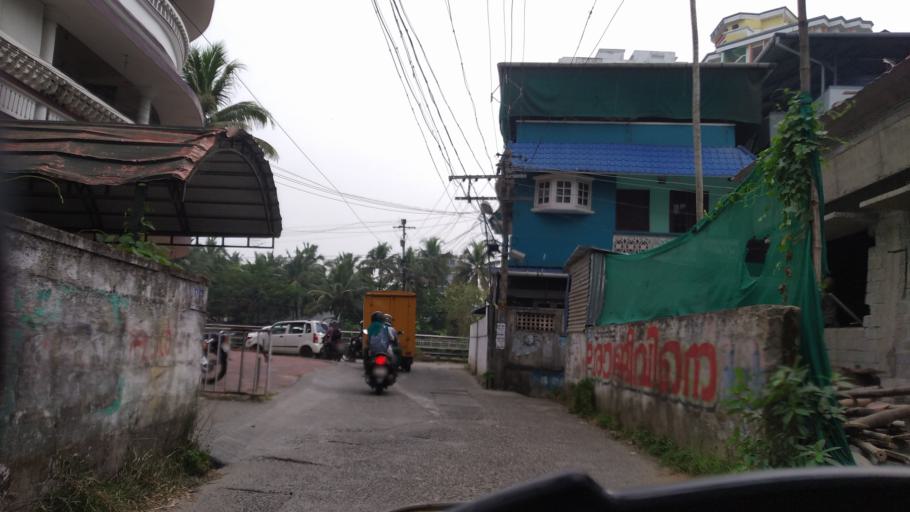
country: IN
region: Kerala
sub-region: Ernakulam
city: Cochin
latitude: 9.9549
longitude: 76.3165
